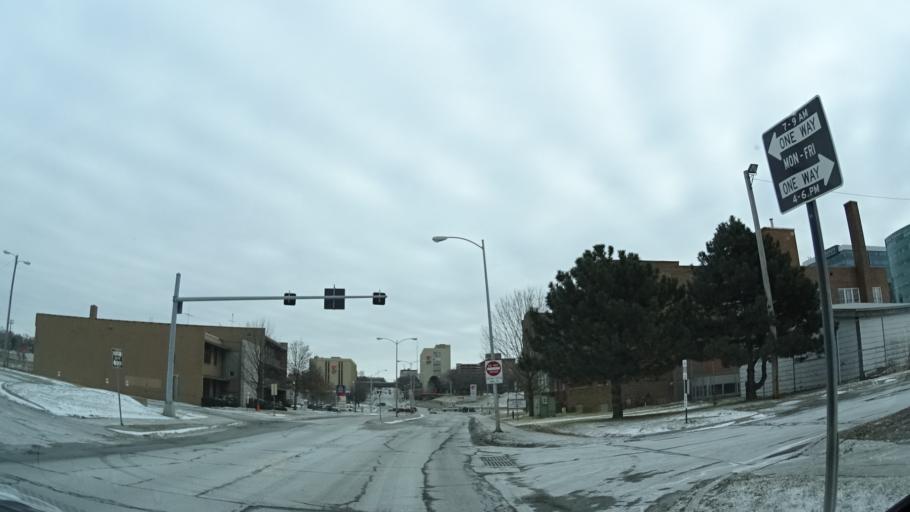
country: US
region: Nebraska
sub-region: Douglas County
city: Omaha
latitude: 41.2578
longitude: -95.9827
